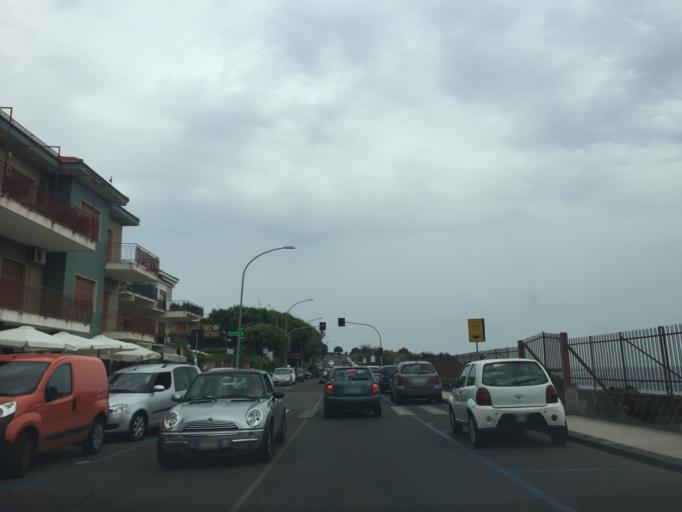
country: IT
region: Sicily
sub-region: Catania
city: Cerza
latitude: 37.5352
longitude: 15.1264
